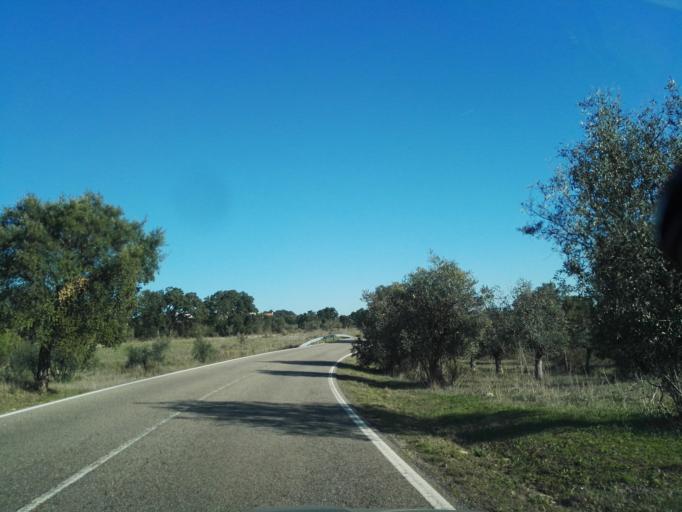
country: PT
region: Santarem
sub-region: Constancia
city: Constancia
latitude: 39.4822
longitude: -8.3124
